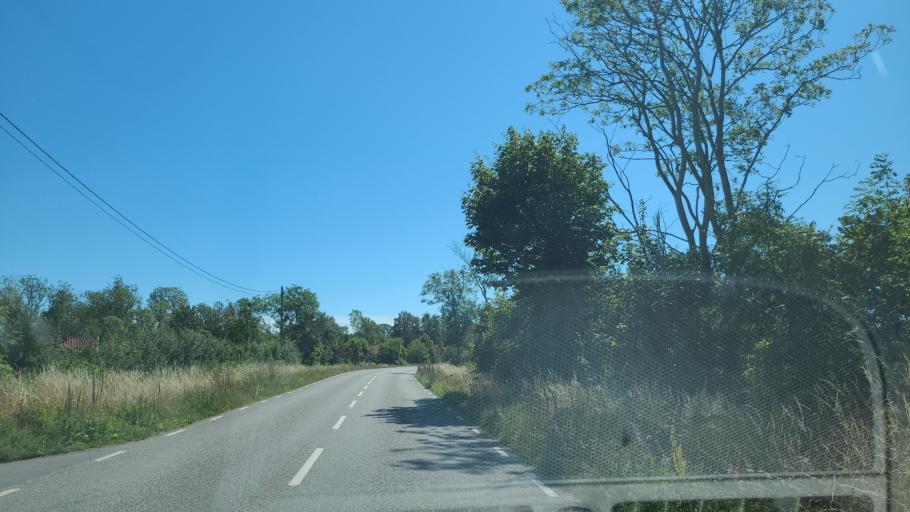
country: SE
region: Kalmar
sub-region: Borgholms Kommun
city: Borgholm
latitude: 56.7720
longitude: 16.5814
